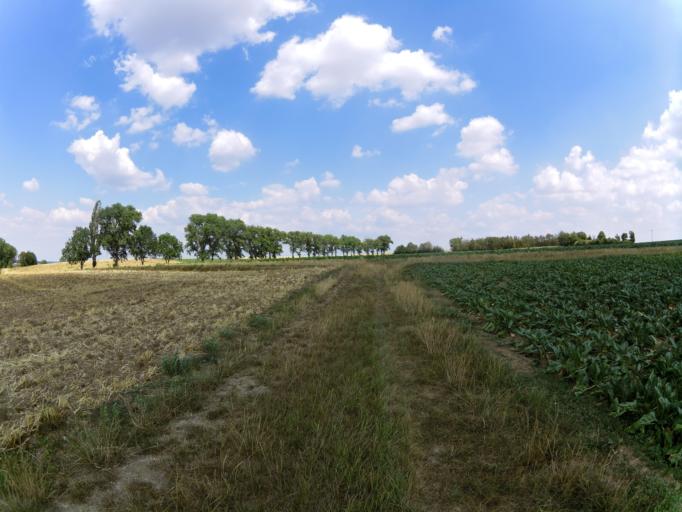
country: DE
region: Bavaria
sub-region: Regierungsbezirk Unterfranken
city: Ochsenfurt
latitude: 49.6418
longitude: 10.0588
